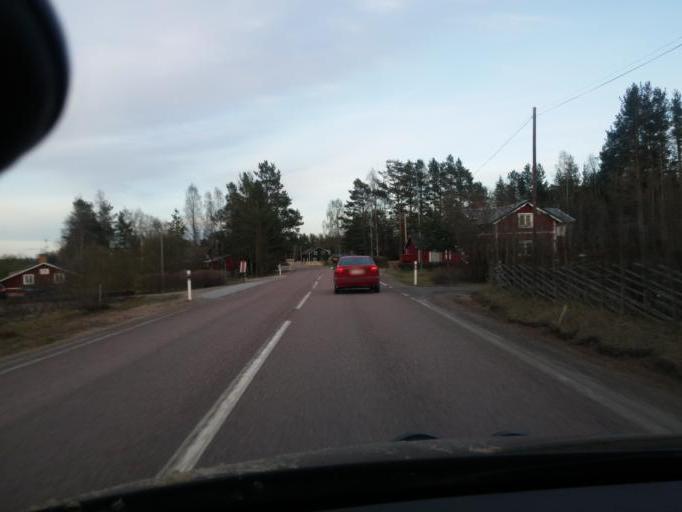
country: SE
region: Gaevleborg
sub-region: Ljusdals Kommun
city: Ljusdal
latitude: 61.8355
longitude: 16.0137
